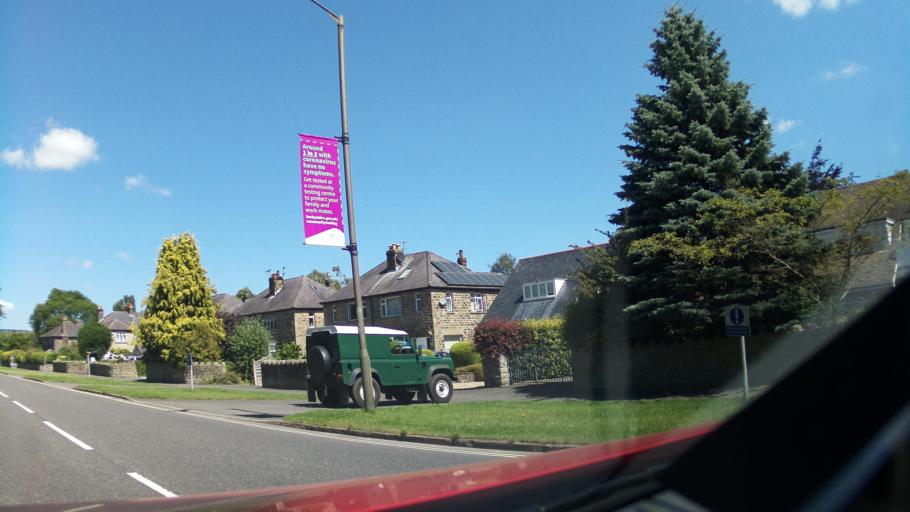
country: GB
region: England
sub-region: Derbyshire
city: Bakewell
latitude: 53.2075
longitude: -1.6693
